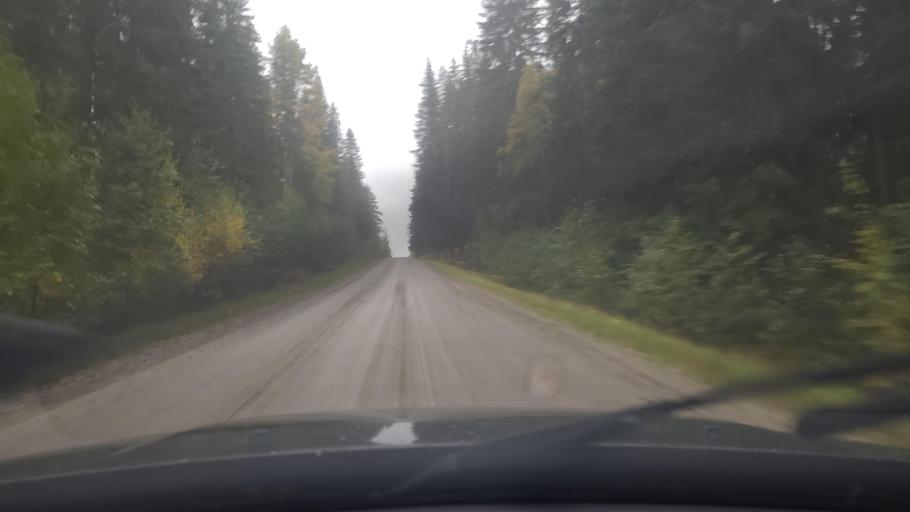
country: FI
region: Northern Savo
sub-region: Varkaus
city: Kangaslampi
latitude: 62.4497
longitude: 28.2961
